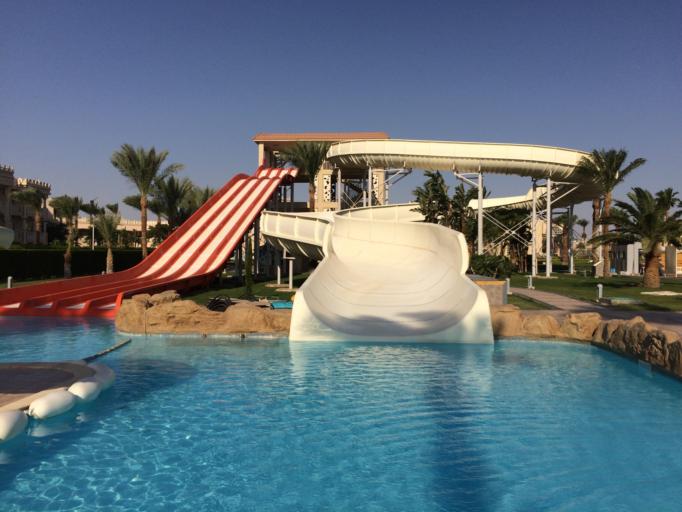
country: EG
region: Red Sea
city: Hurghada
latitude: 27.1216
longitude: 33.8263
